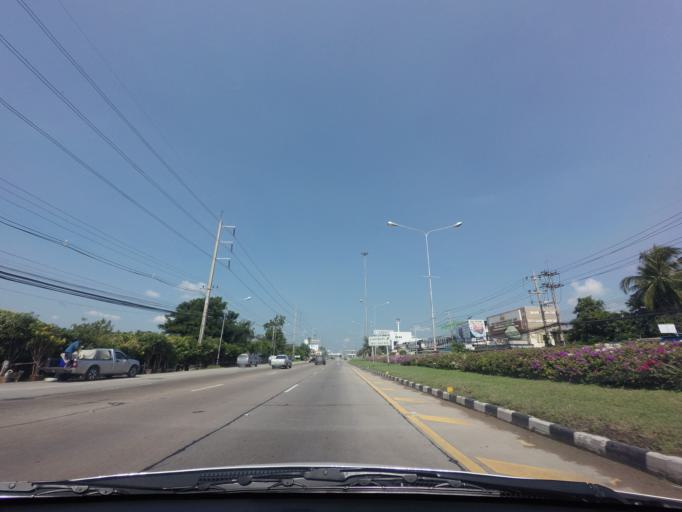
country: TH
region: Nakhon Pathom
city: Nakhon Chai Si
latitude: 13.7892
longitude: 100.1716
